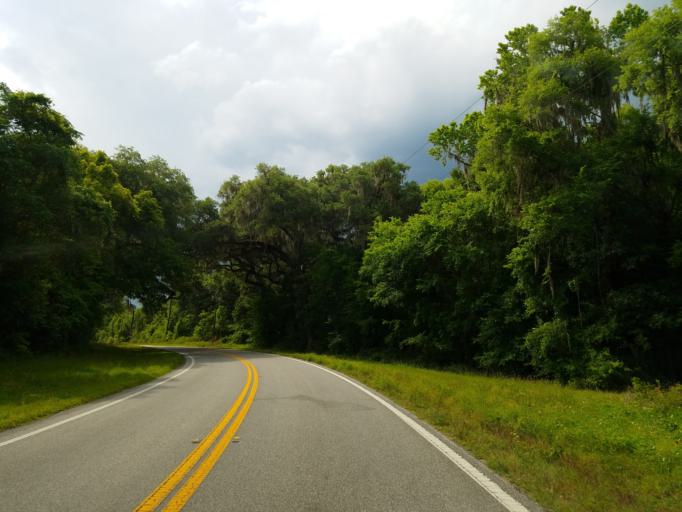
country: US
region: Florida
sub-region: Hernando County
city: Brooksville
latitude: 28.5541
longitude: -82.3547
